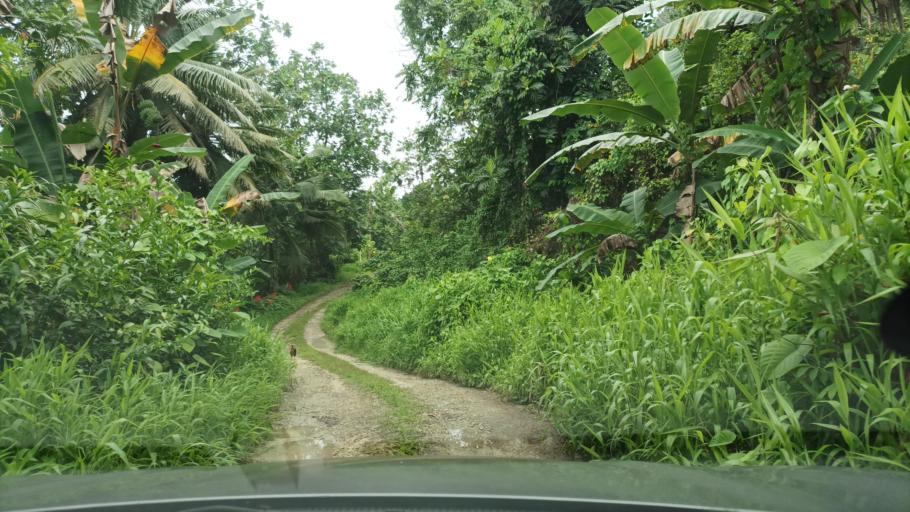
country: FM
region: Pohnpei
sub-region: Kolonia Municipality
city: Kolonia
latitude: 6.9388
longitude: 158.2657
